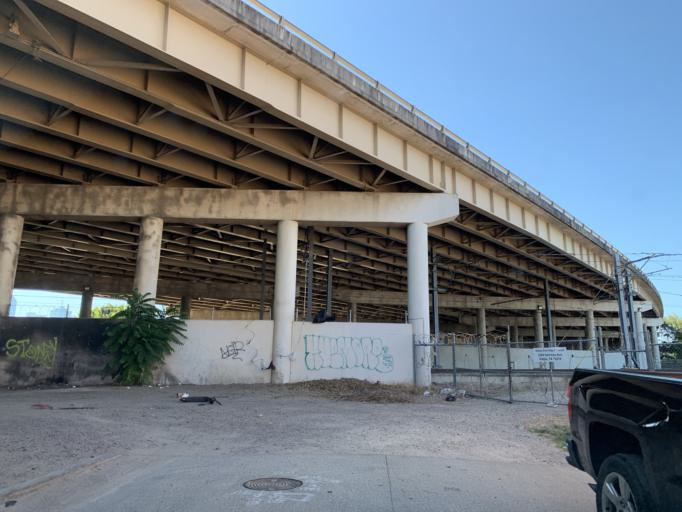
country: US
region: Texas
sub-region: Dallas County
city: Dallas
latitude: 32.7728
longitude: -96.7778
